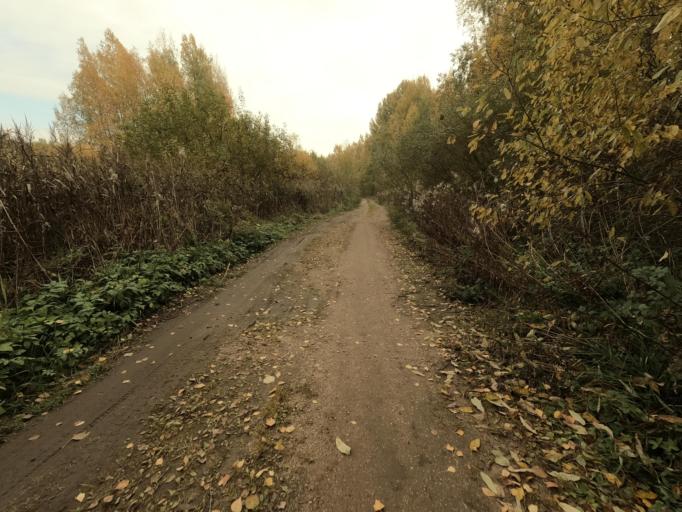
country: RU
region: Novgorod
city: Pankovka
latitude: 58.8722
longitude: 30.8912
